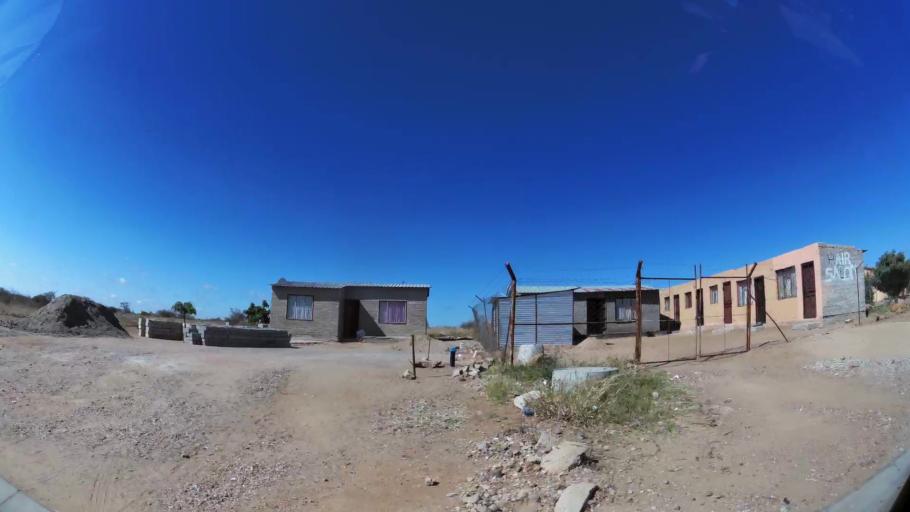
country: ZA
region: Limpopo
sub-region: Capricorn District Municipality
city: Polokwane
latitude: -23.8771
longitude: 29.4127
